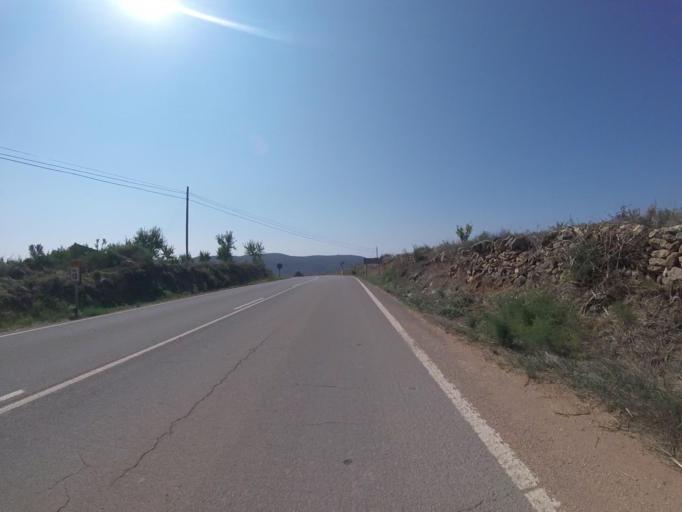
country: ES
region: Valencia
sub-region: Provincia de Castello
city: Adzaneta
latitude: 40.2309
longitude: -0.1765
